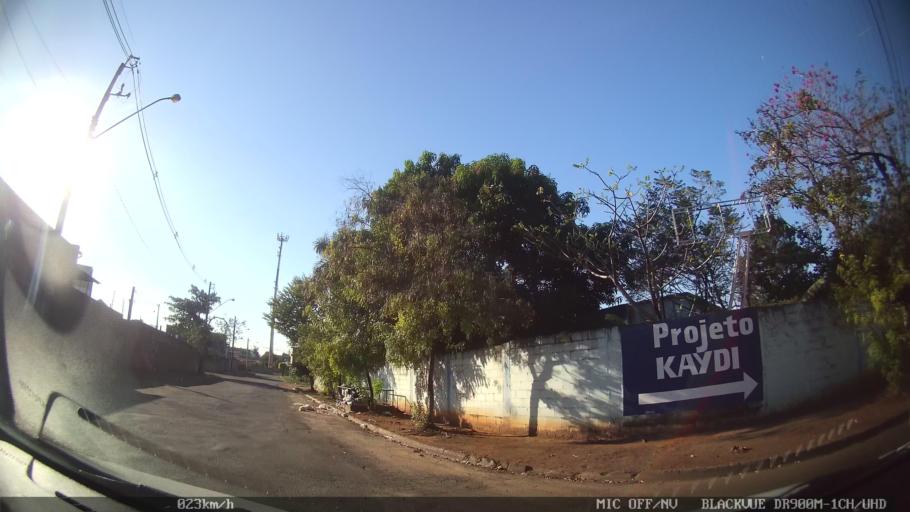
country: BR
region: Sao Paulo
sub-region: Nova Odessa
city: Nova Odessa
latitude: -22.7782
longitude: -47.2892
